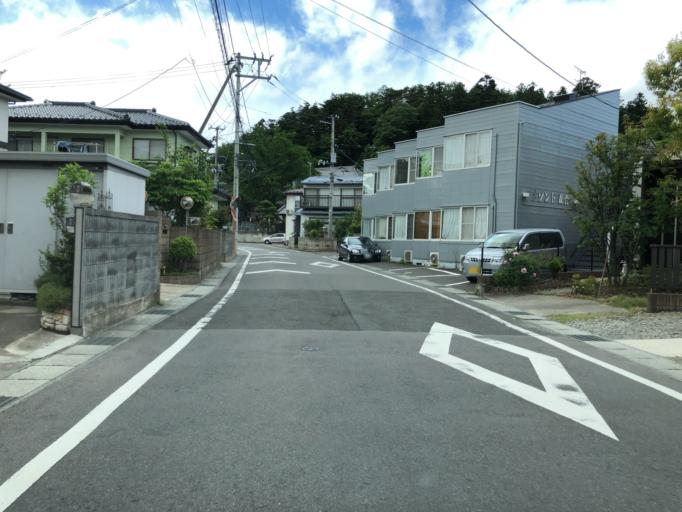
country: JP
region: Fukushima
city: Fukushima-shi
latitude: 37.7651
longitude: 140.4515
